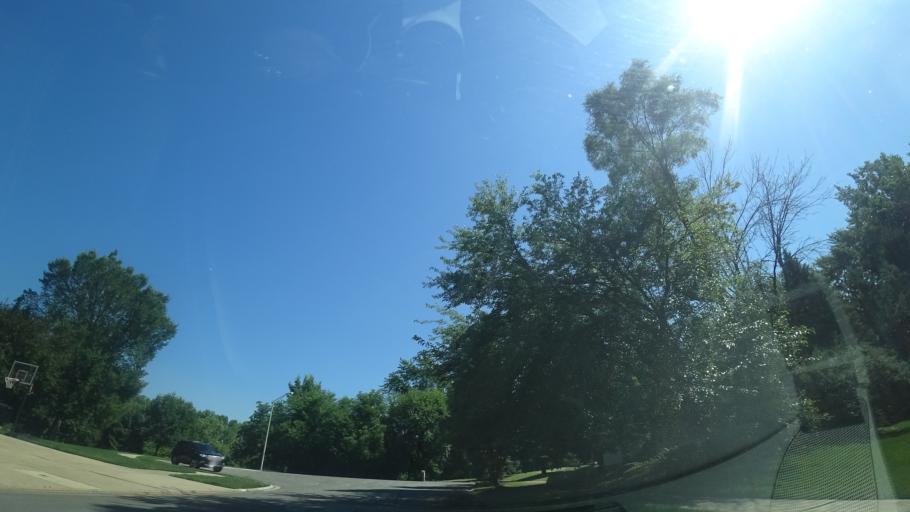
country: US
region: Illinois
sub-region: Will County
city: Mokena
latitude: 41.5675
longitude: -87.9014
